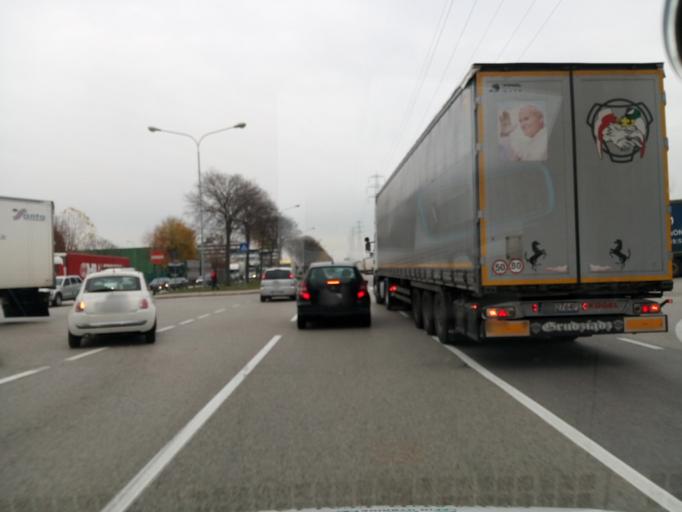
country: IT
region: Veneto
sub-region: Provincia di Padova
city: Noventa
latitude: 45.3929
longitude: 11.9388
